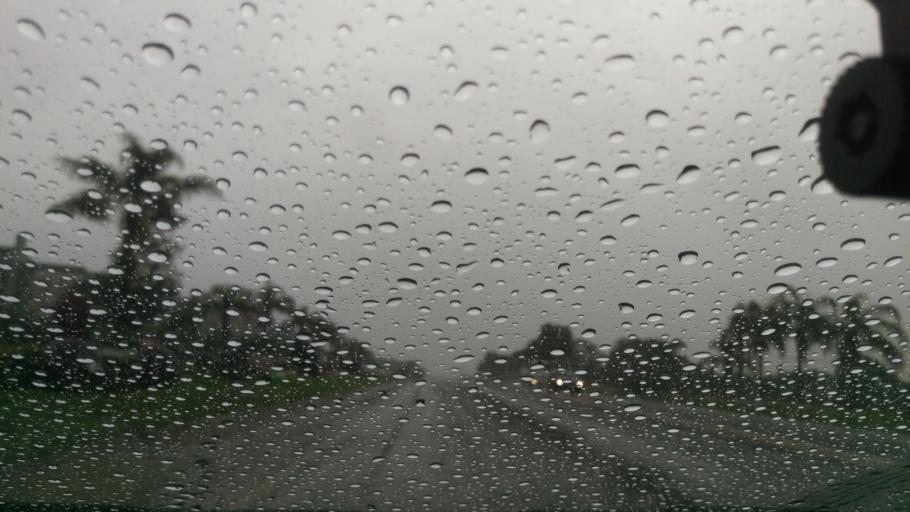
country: ZA
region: Gauteng
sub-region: West Rand District Municipality
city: Muldersdriseloop
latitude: -26.0500
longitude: 27.9507
